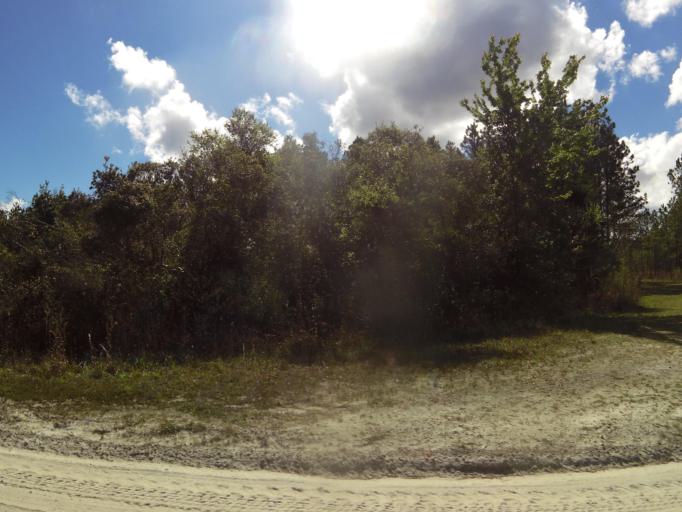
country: US
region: Florida
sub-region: Clay County
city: Green Cove Springs
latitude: 29.8680
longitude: -81.7110
